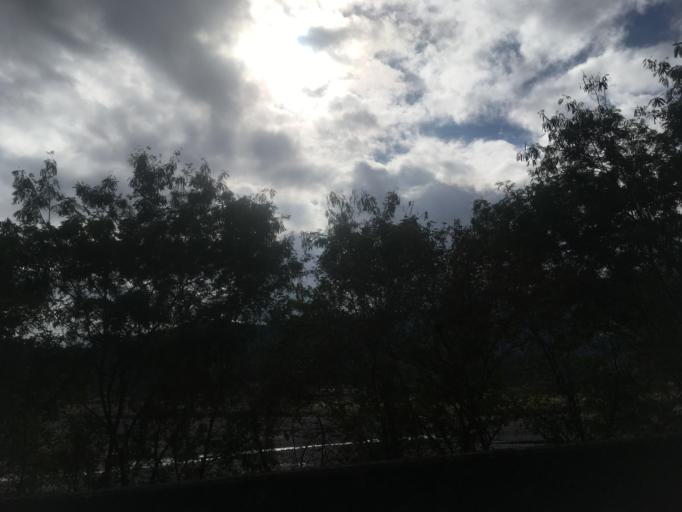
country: TW
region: Taiwan
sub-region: Yilan
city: Yilan
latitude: 24.6519
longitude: 121.5782
